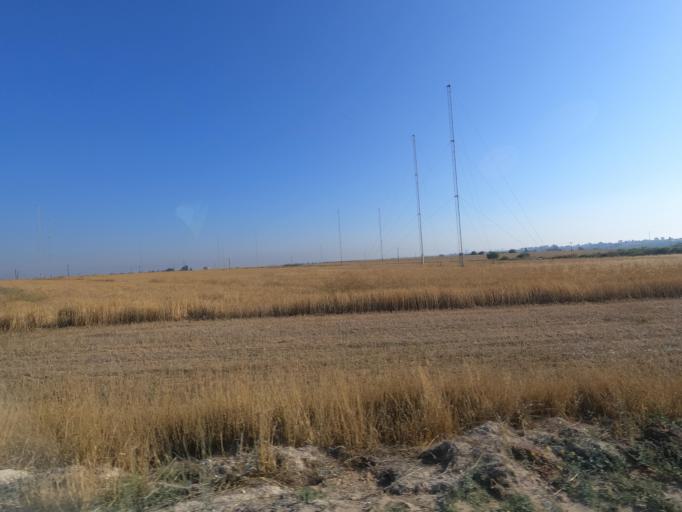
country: CY
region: Ammochostos
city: Acheritou
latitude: 35.0938
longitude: 33.8935
